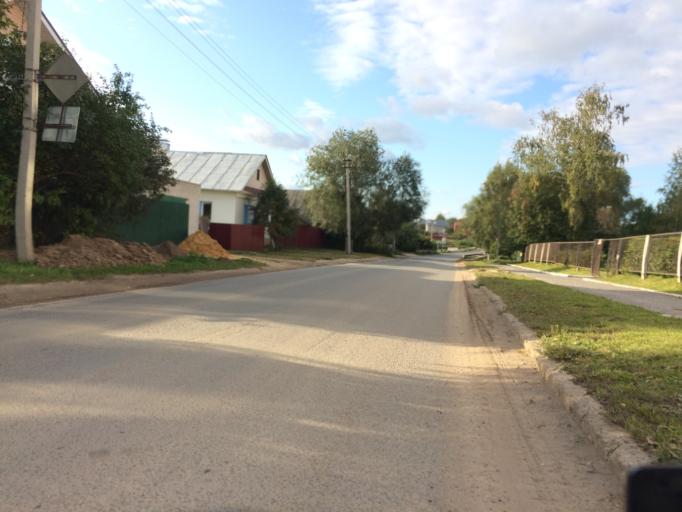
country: RU
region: Mariy-El
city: Yoshkar-Ola
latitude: 56.6469
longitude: 47.9815
